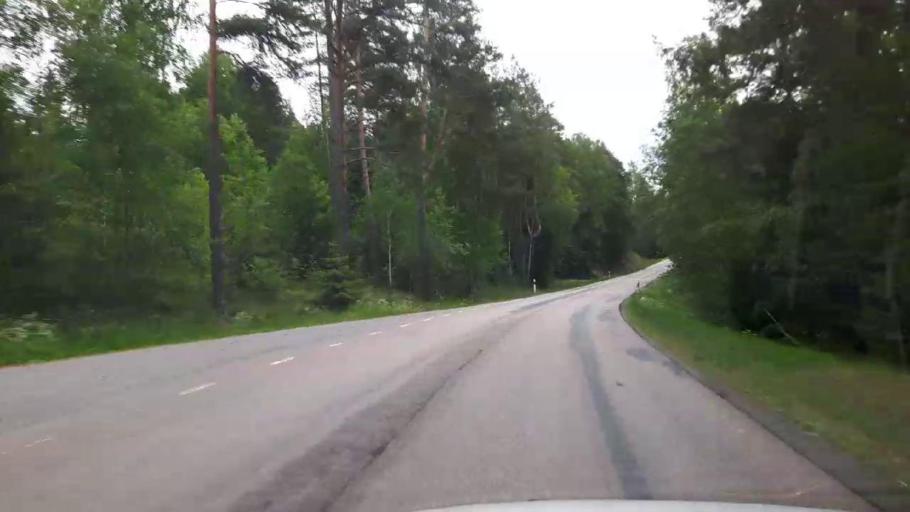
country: SE
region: Vaestmanland
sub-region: Kopings Kommun
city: Kolsva
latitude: 59.6460
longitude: 15.7868
